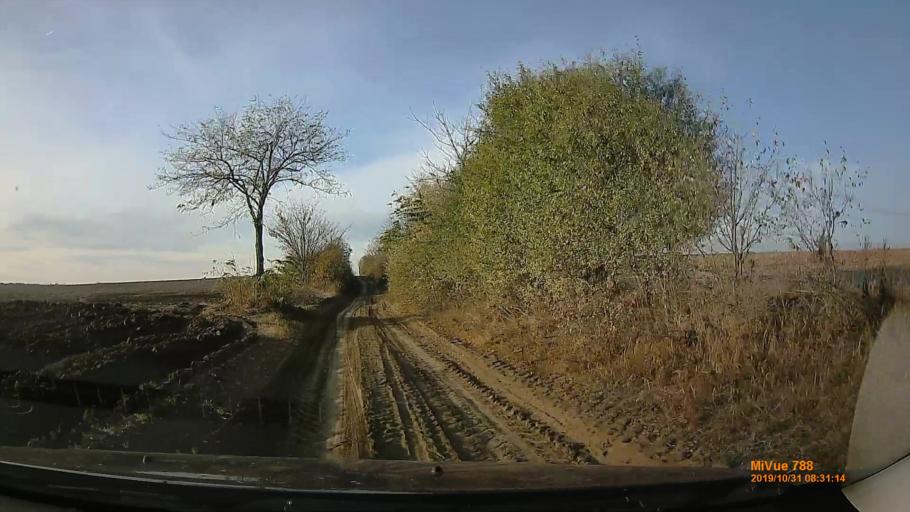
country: HU
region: Pest
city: Tapiobicske
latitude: 47.3484
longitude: 19.6666
